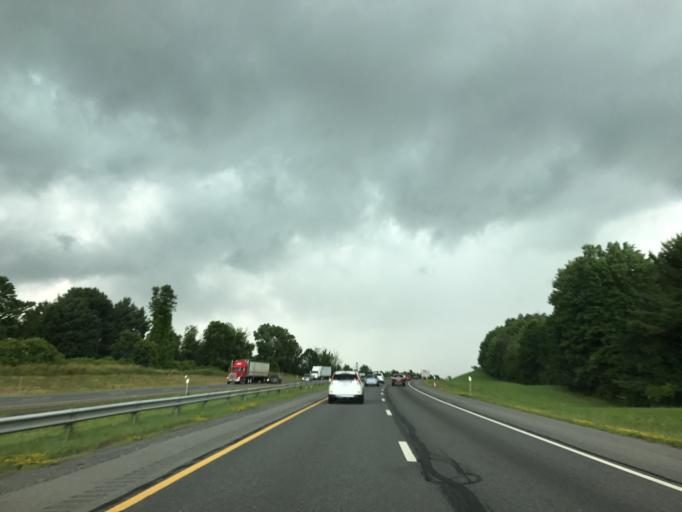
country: US
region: New York
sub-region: Albany County
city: Ravena
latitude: 42.4507
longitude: -73.8111
